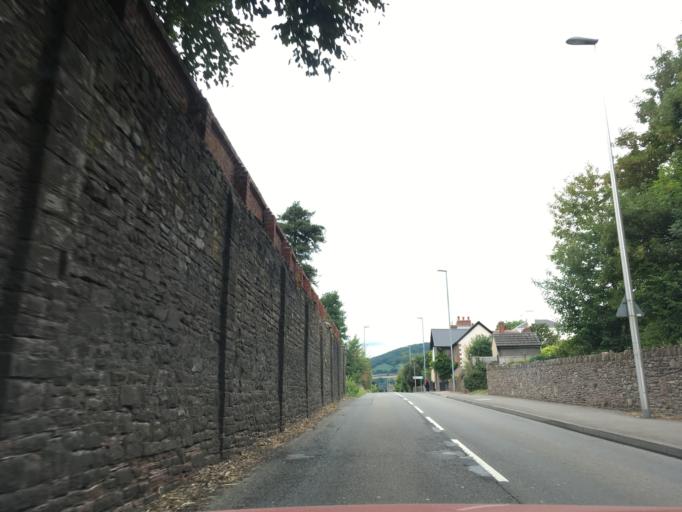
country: GB
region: Wales
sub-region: Monmouthshire
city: Abergavenny
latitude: 51.8149
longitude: -3.0119
